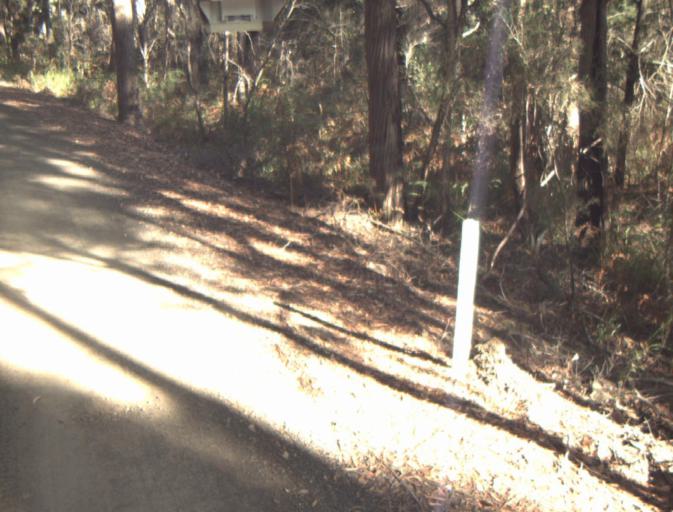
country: AU
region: Tasmania
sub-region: Launceston
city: Mayfield
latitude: -41.3000
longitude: 147.1881
